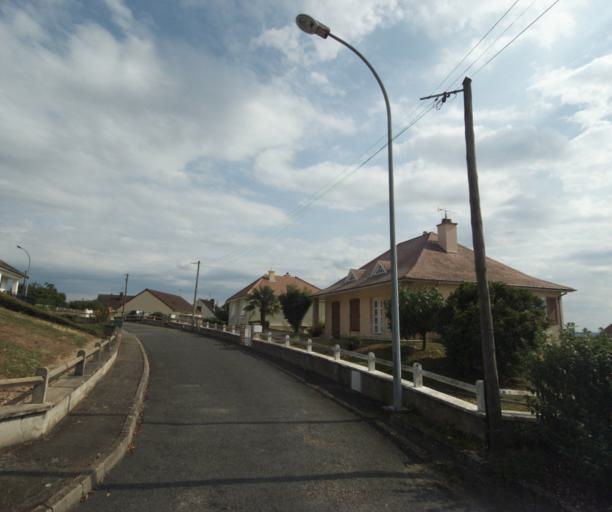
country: FR
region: Bourgogne
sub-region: Departement de Saone-et-Loire
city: Gueugnon
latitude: 46.6038
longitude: 4.0789
